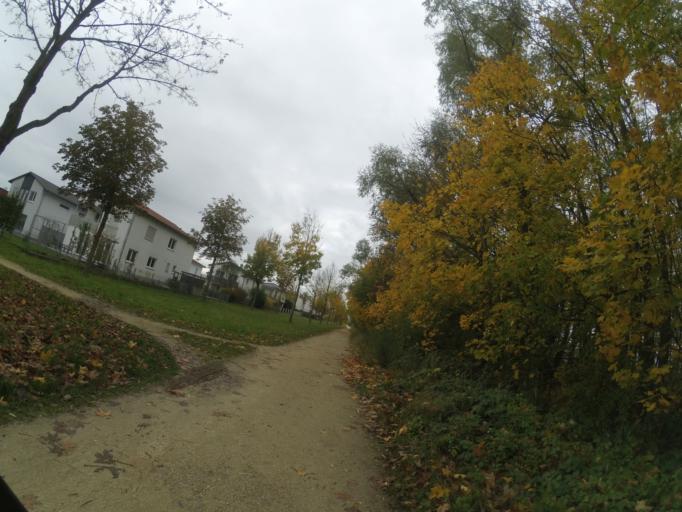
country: DE
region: Bavaria
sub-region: Swabia
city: Neu-Ulm
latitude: 48.3741
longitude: 10.0158
